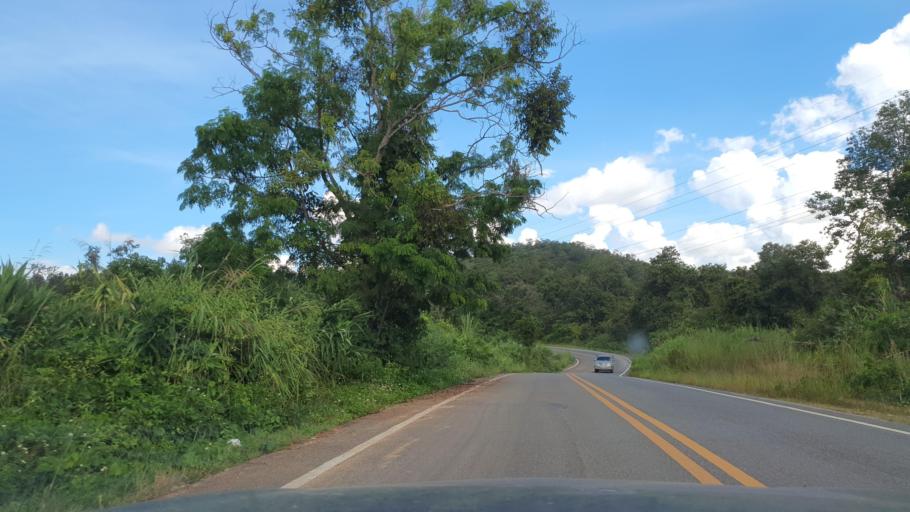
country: TH
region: Chiang Rai
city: Wiang Pa Pao
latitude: 19.3134
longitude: 99.4240
